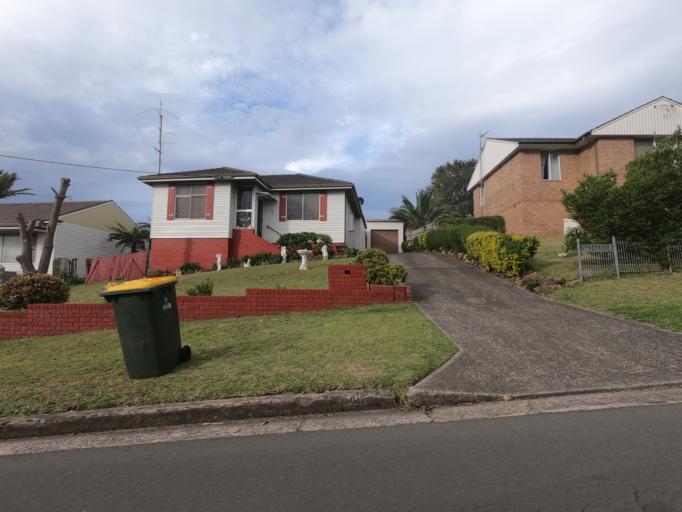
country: AU
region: New South Wales
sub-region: Wollongong
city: Berkeley
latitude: -34.4773
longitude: 150.8414
